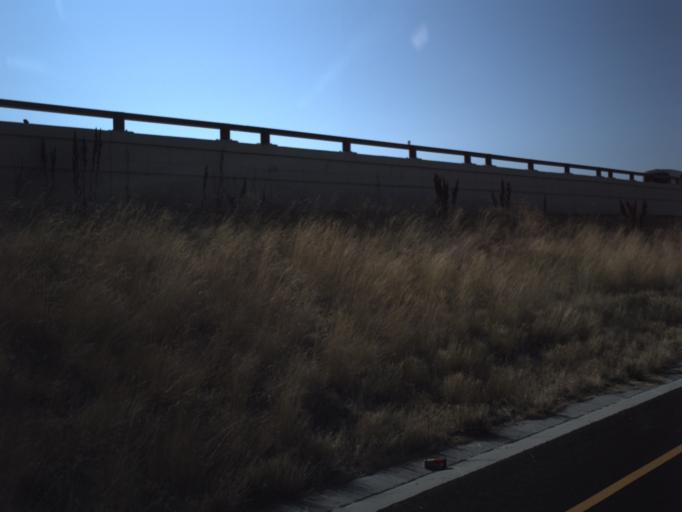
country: US
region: Utah
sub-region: Davis County
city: Centerville
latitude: 40.9233
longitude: -111.9000
